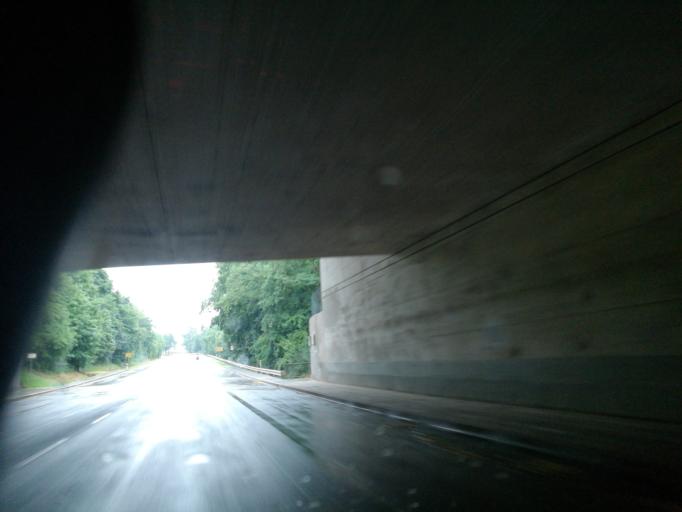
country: DE
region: Bavaria
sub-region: Regierungsbezirk Mittelfranken
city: Obermichelbach
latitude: 49.5311
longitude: 10.9639
